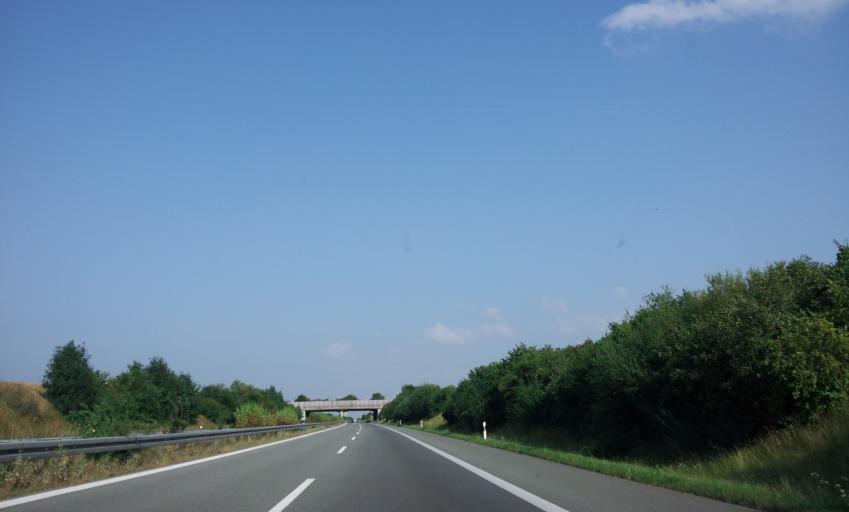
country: DE
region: Mecklenburg-Vorpommern
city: Gross Miltzow
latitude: 53.5635
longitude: 13.4901
